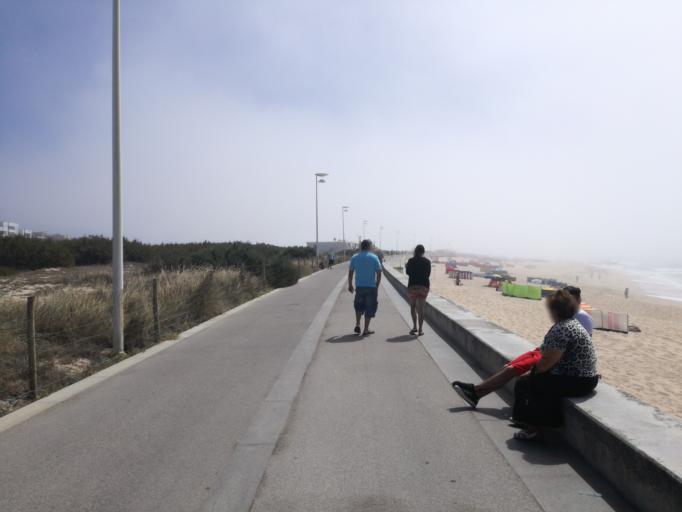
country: PT
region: Porto
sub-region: Vila do Conde
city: Vila do Conde
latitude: 41.3469
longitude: -8.7535
